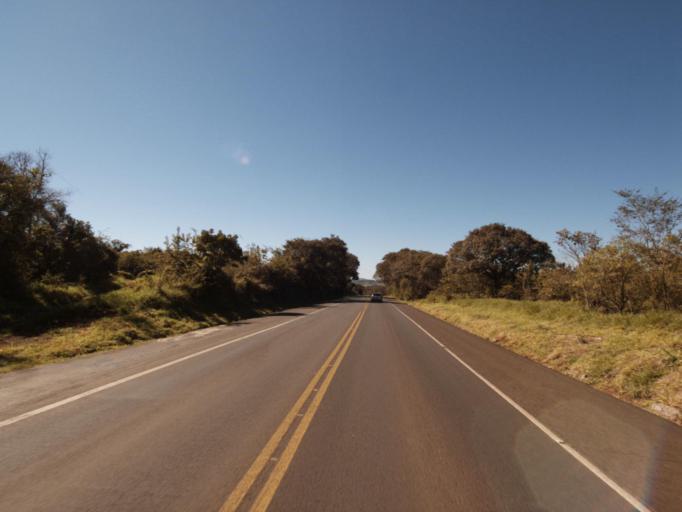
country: BR
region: Santa Catarina
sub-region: Chapeco
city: Chapeco
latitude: -26.9020
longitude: -52.8915
